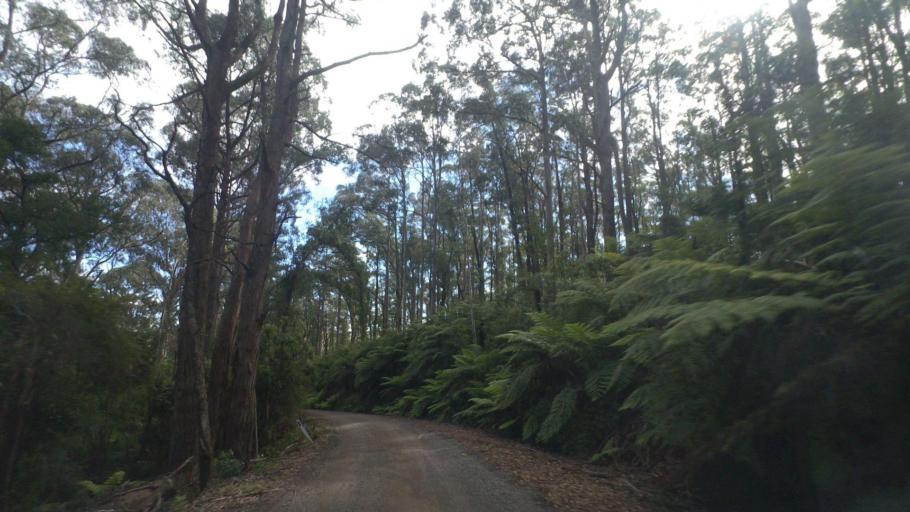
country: AU
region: Victoria
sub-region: Cardinia
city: Gembrook
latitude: -37.9192
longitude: 145.6145
